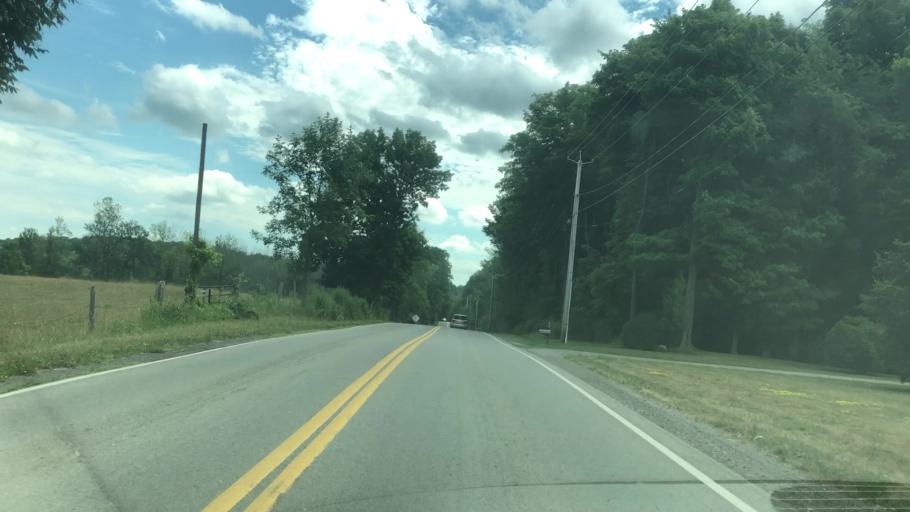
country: US
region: New York
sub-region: Wayne County
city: Macedon
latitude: 43.0866
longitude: -77.3594
